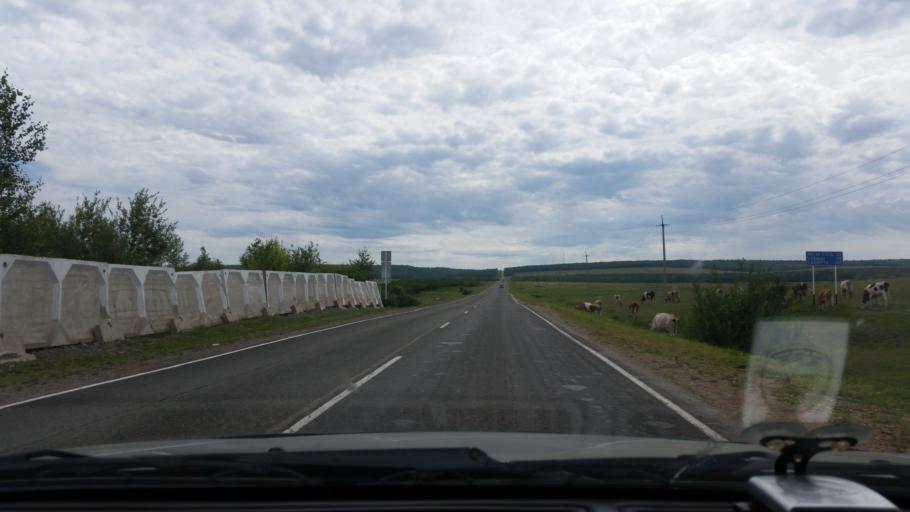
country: RU
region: Irkutsk
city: Bayanday
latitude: 53.0522
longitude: 105.5281
